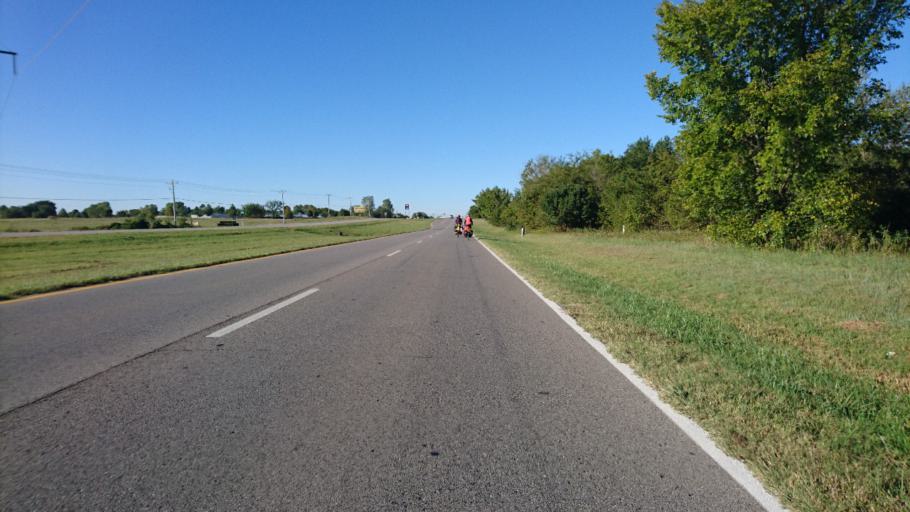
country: US
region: Oklahoma
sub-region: Rogers County
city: Verdigris
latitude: 36.2545
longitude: -95.6635
